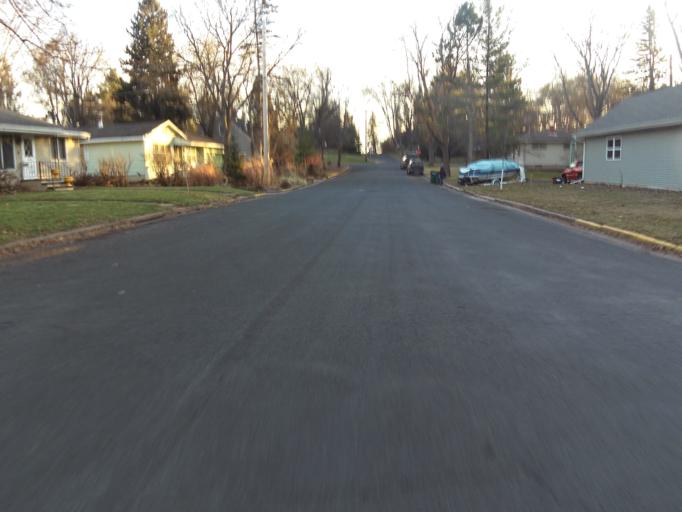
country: US
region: Wisconsin
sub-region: Pierce County
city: River Falls
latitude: 44.8562
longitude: -92.6167
